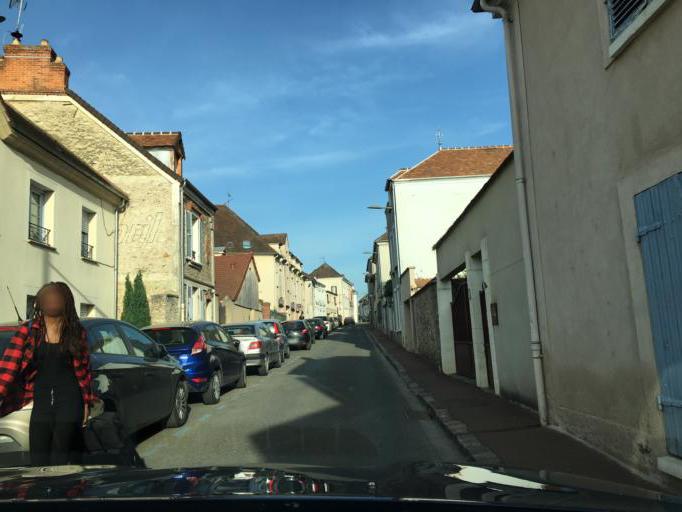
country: FR
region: Centre
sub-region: Departement d'Eure-et-Loir
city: Epernon
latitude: 48.6086
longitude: 1.6790
